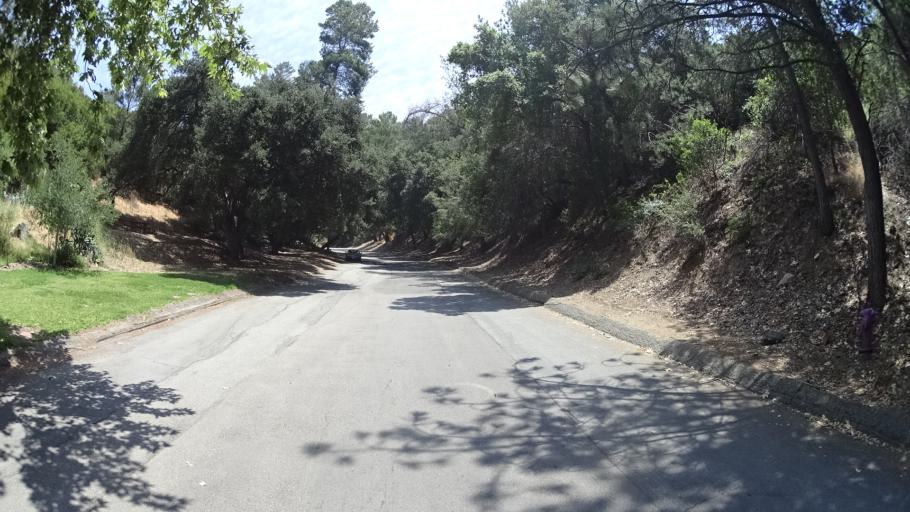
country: US
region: California
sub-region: Los Angeles County
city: Burbank
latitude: 34.2028
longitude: -118.2978
